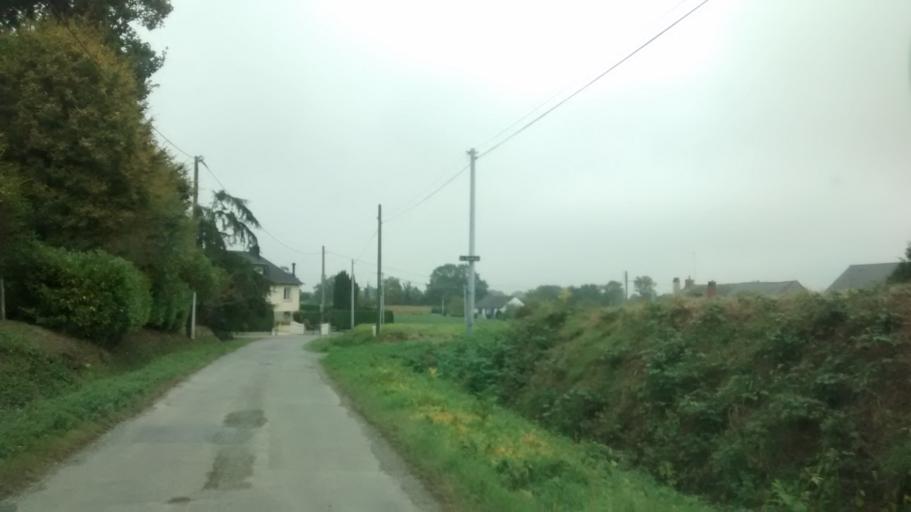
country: FR
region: Brittany
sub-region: Departement d'Ille-et-Vilaine
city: Cintre
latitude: 48.1173
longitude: -1.8940
